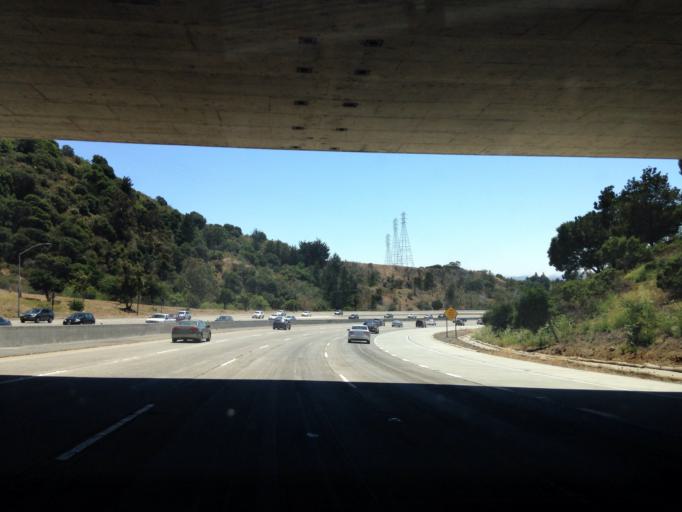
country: US
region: California
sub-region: Alameda County
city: Piedmont
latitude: 37.8508
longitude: -122.2231
